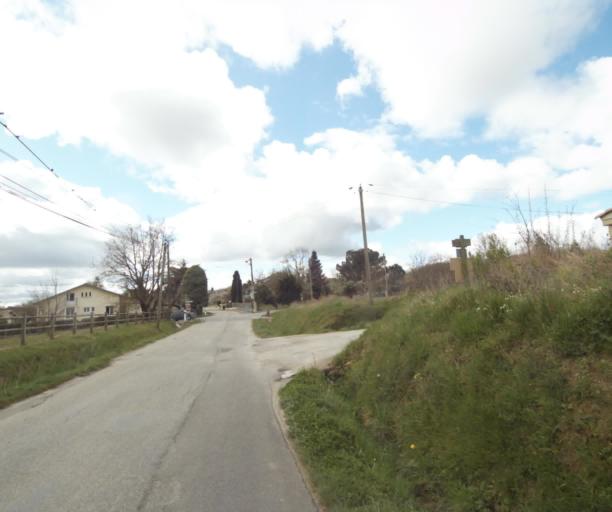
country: FR
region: Midi-Pyrenees
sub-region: Departement de l'Ariege
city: Saverdun
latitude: 43.2246
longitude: 1.5720
